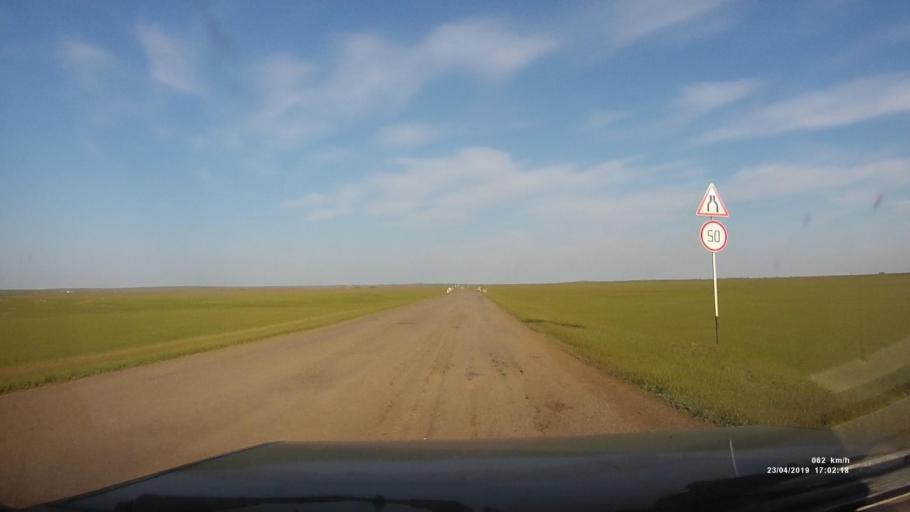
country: RU
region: Kalmykiya
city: Priyutnoye
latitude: 46.2930
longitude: 43.4161
